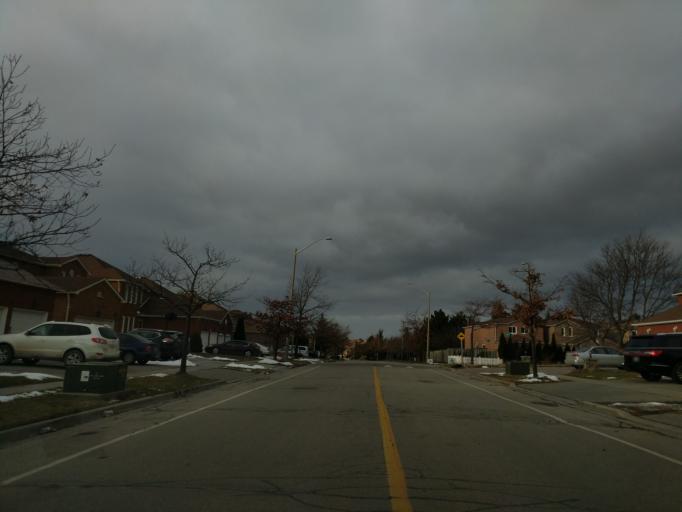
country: CA
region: Ontario
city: Markham
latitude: 43.8428
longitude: -79.2684
